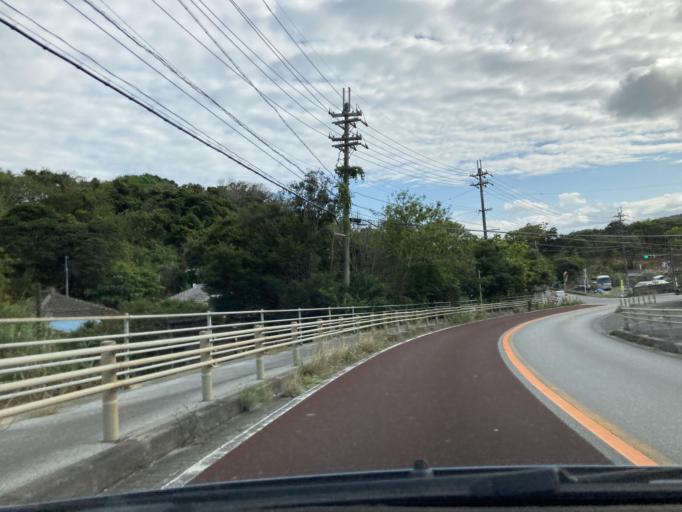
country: JP
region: Okinawa
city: Nago
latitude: 26.6578
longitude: 127.9843
